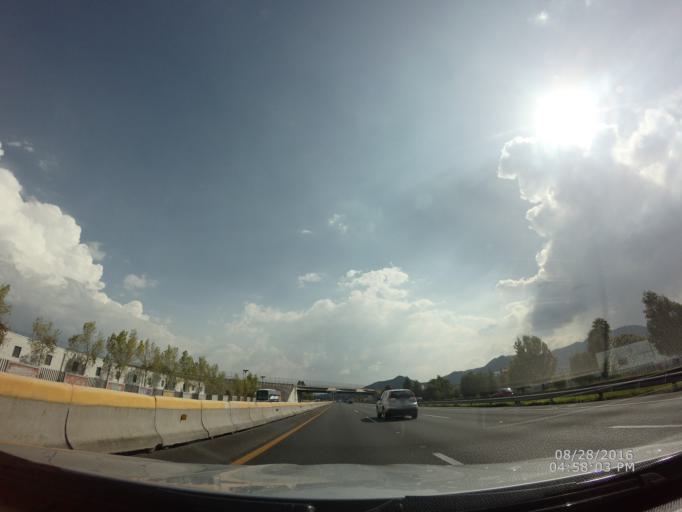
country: MX
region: Mexico
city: Ecatepec
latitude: 19.6108
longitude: -99.0339
